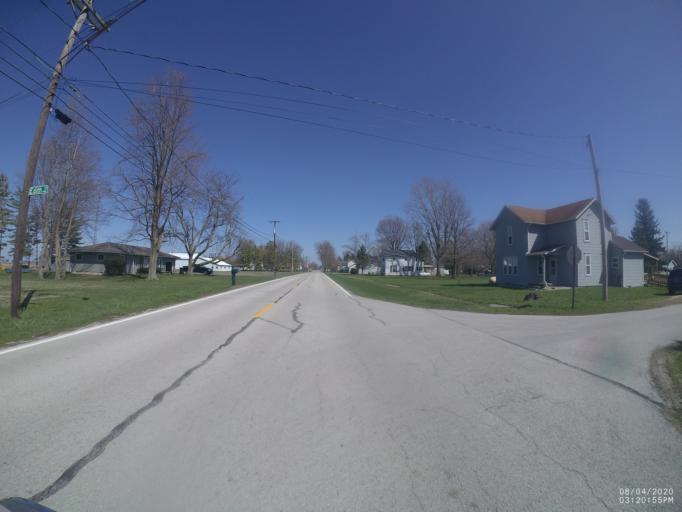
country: US
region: Ohio
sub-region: Sandusky County
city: Stony Prairie
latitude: 41.2677
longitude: -83.2547
